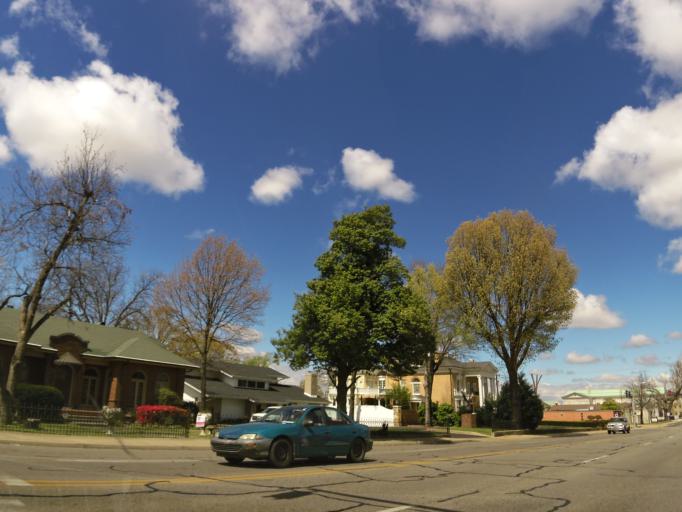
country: US
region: Arkansas
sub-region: Craighead County
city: Jonesboro
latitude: 35.8329
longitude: -90.7051
